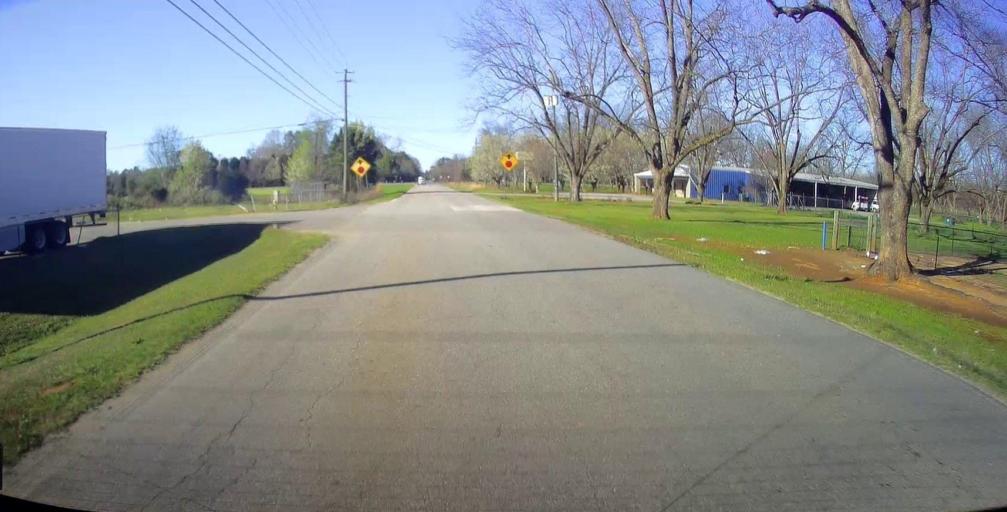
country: US
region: Georgia
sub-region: Peach County
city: Fort Valley
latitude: 32.5756
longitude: -83.8930
